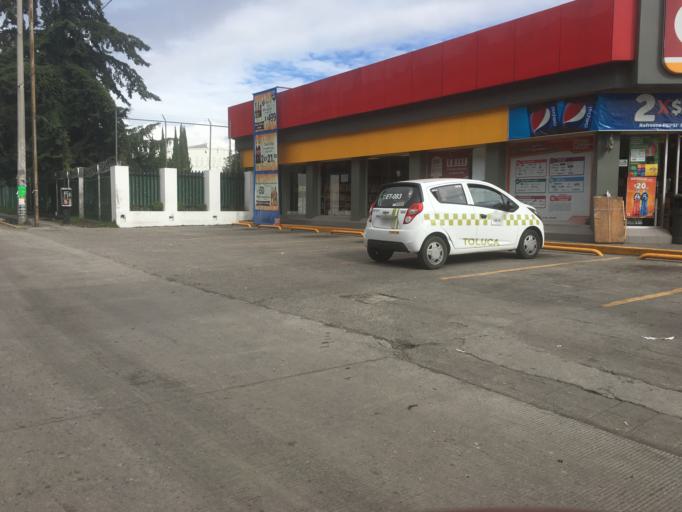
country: MX
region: Mexico
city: Santa Maria Totoltepec
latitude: 19.2879
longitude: -99.5944
